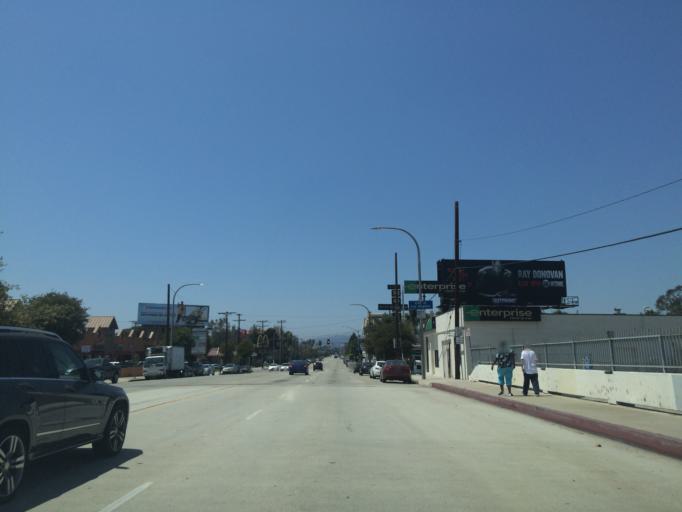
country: US
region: California
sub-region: Los Angeles County
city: Culver City
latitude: 33.9997
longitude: -118.4010
